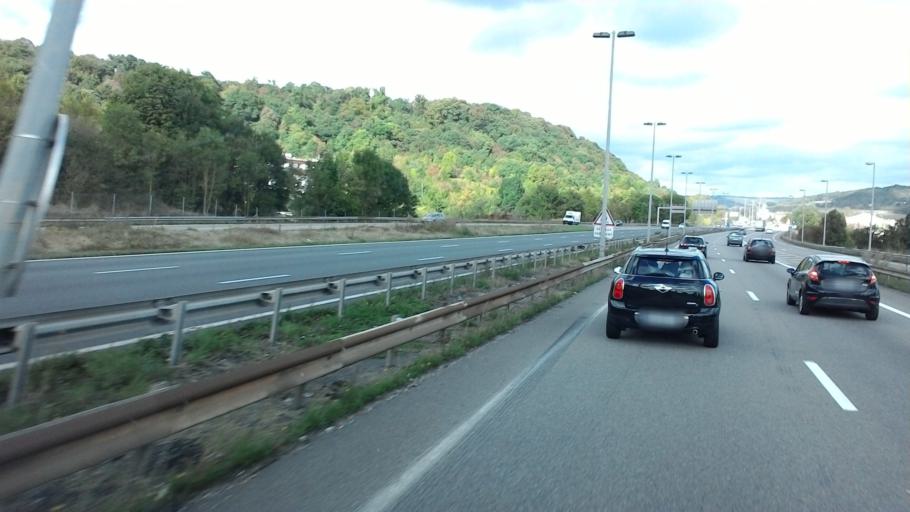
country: FR
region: Lorraine
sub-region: Departement de Meurthe-et-Moselle
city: Maxeville
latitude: 48.7170
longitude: 6.1636
